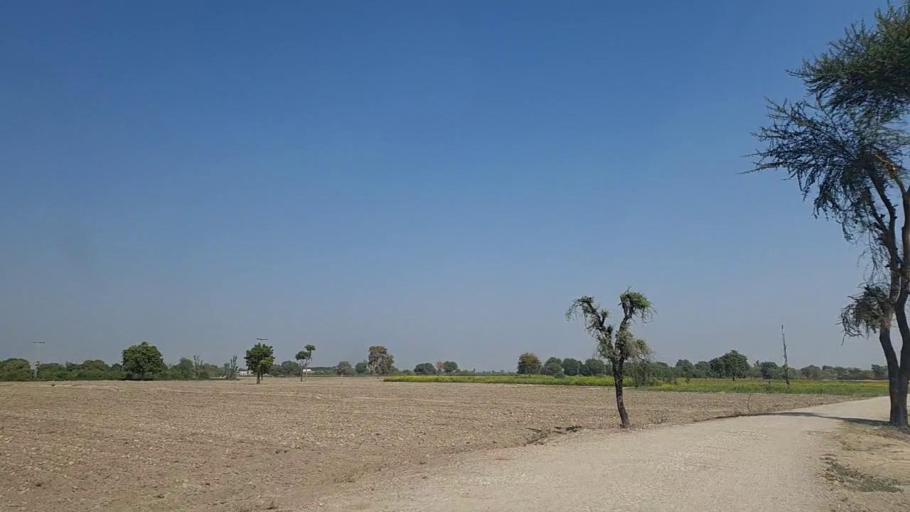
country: PK
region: Sindh
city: Naukot
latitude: 24.8572
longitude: 69.4156
